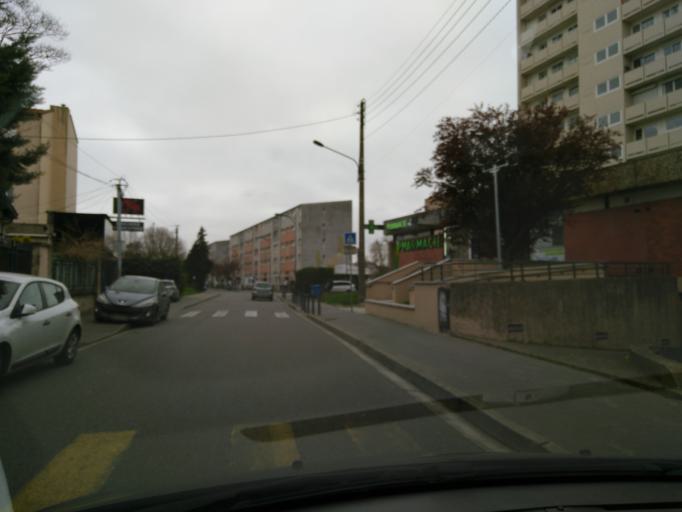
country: FR
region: Midi-Pyrenees
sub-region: Departement de la Haute-Garonne
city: Toulouse
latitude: 43.5808
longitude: 1.4584
